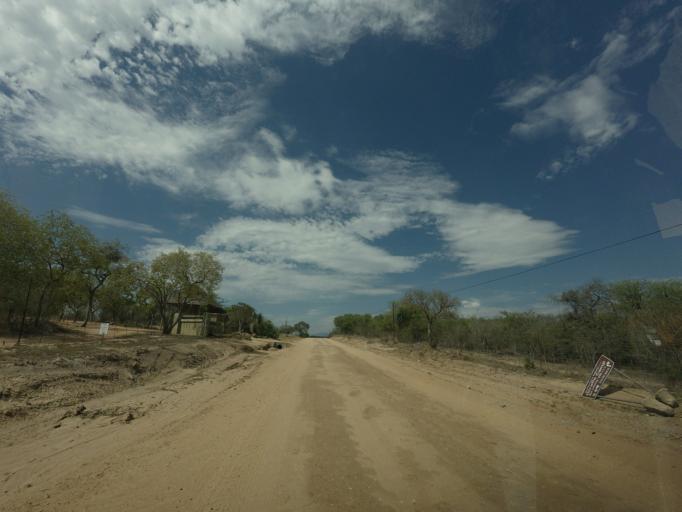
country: ZA
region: Limpopo
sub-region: Mopani District Municipality
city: Hoedspruit
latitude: -24.5157
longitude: 31.0981
